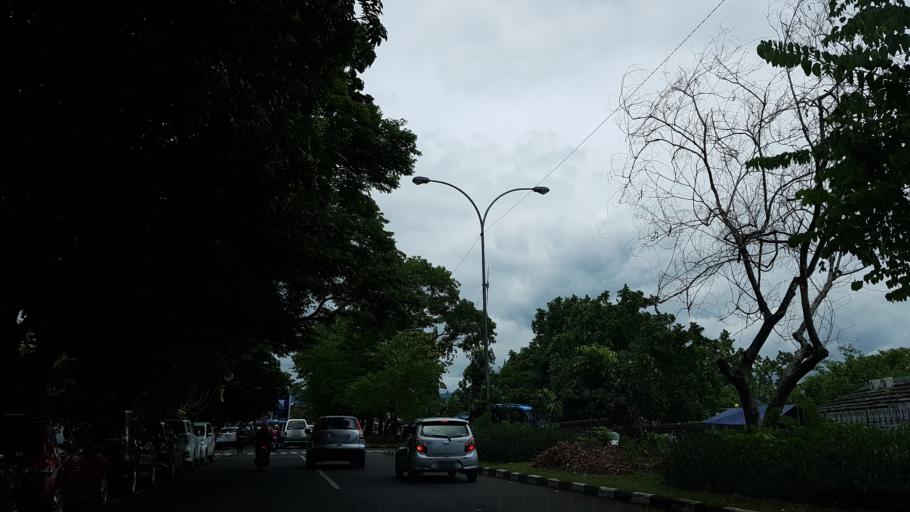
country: ID
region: West Java
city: Bandung
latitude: -6.8939
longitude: 107.6179
